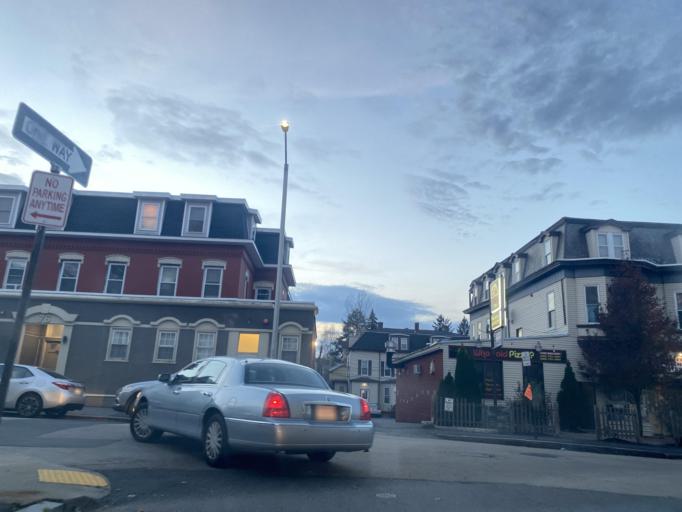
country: US
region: Massachusetts
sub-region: Worcester County
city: Worcester
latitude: 42.2680
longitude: -71.8085
